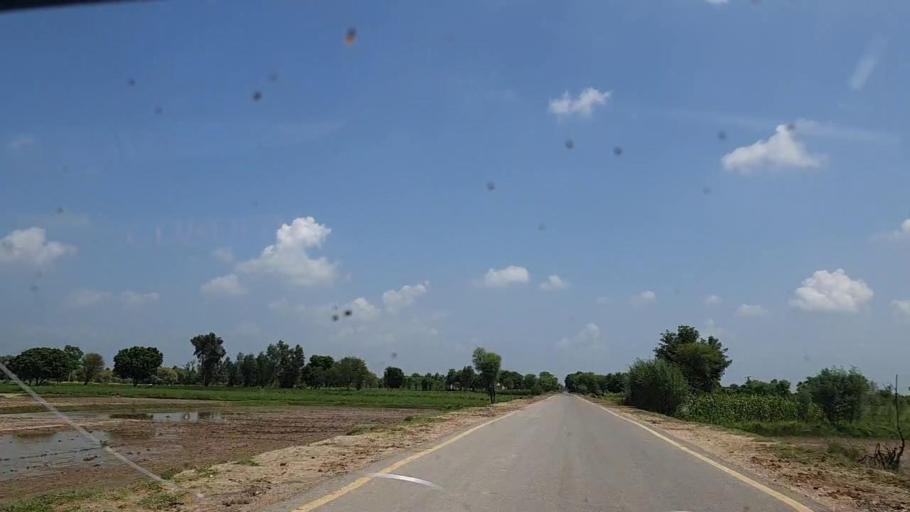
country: PK
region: Sindh
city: Tharu Shah
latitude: 26.9676
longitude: 68.0940
